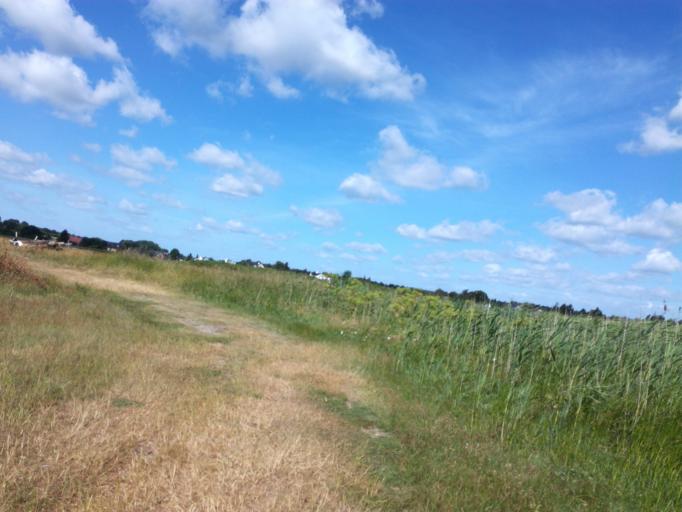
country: DK
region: South Denmark
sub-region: Fredericia Kommune
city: Fredericia
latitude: 55.6275
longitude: 9.7465
